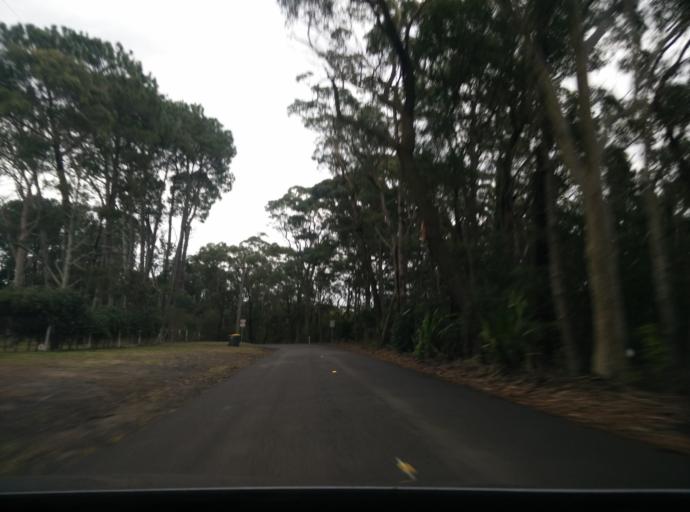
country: AU
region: New South Wales
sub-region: Gosford Shire
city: Narara
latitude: -33.3645
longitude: 151.3153
